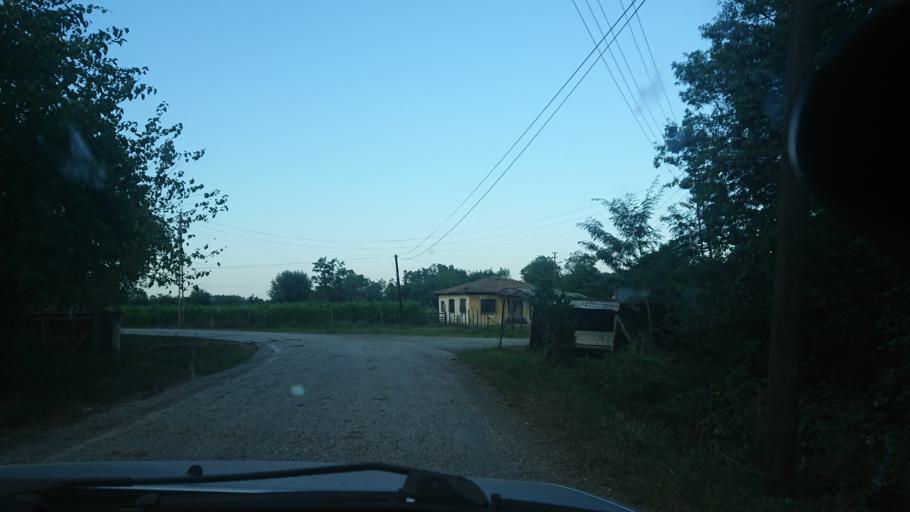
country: TR
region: Samsun
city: Dikbiyik
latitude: 41.1785
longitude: 36.5466
